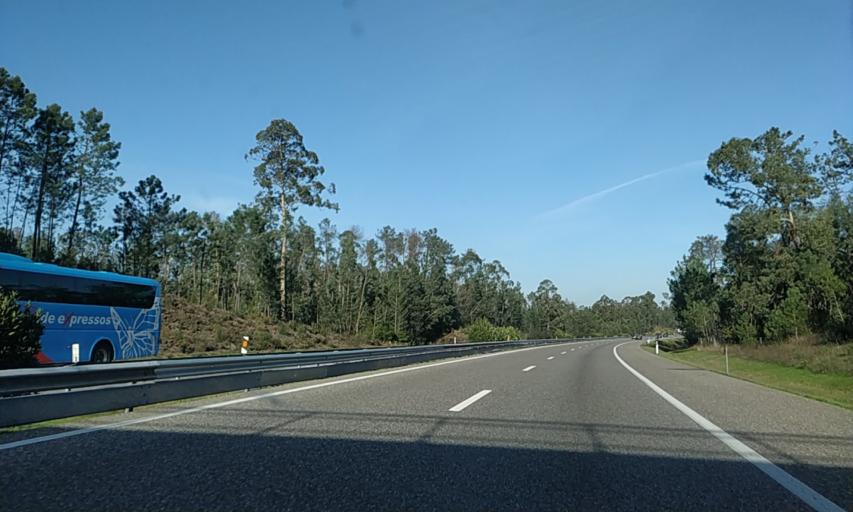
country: PT
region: Coimbra
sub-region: Soure
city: Soure
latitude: 40.0042
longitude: -8.6070
